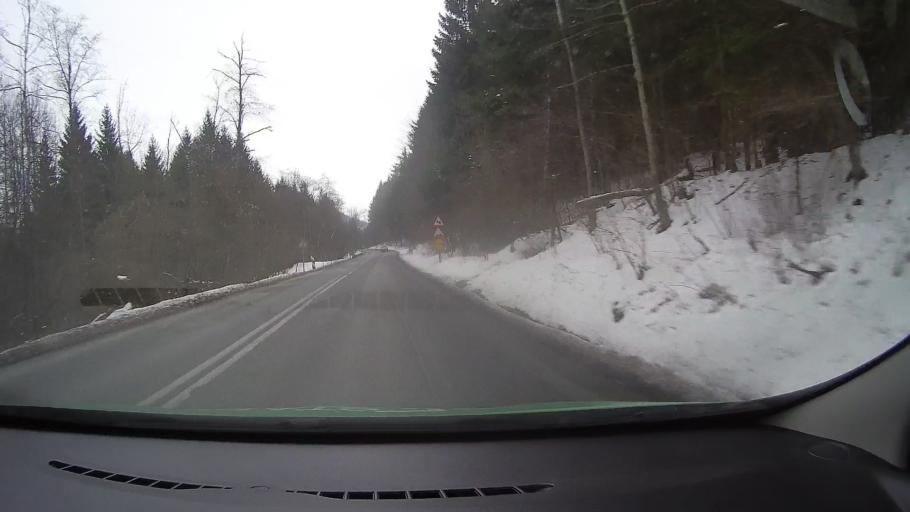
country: RO
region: Brasov
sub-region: Oras Predeal
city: Predeal
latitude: 45.5220
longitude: 25.5053
